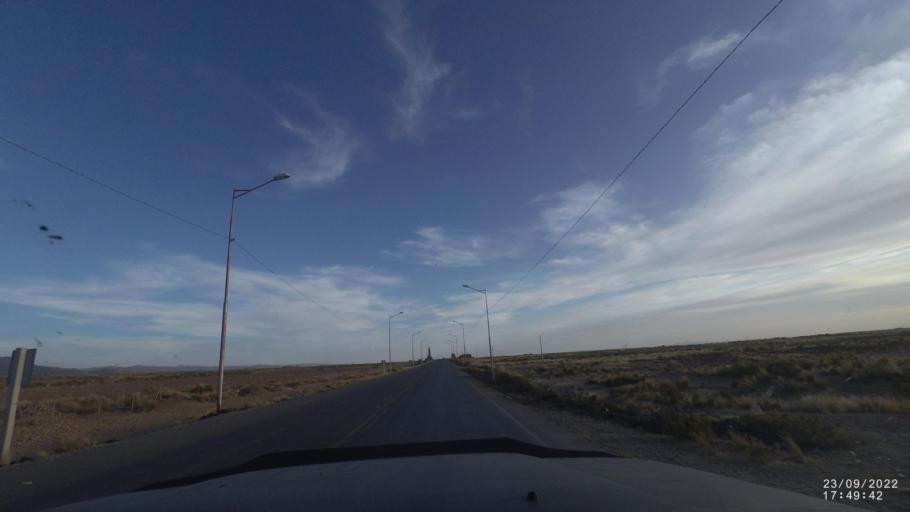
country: BO
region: Oruro
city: Challapata
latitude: -19.0232
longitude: -66.7765
